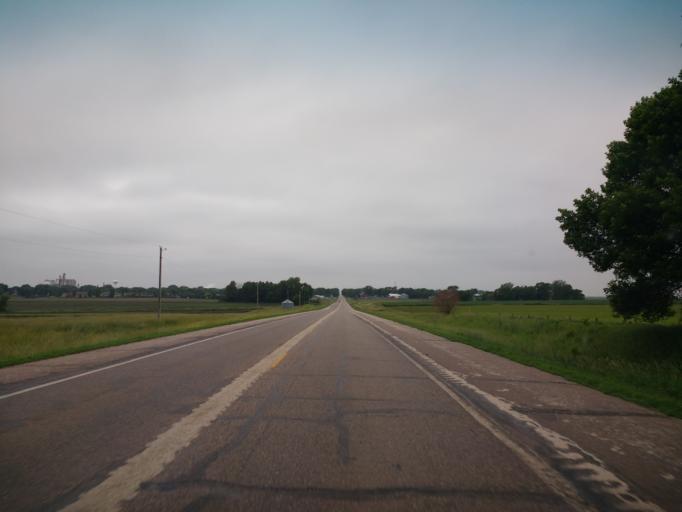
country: US
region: Iowa
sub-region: O'Brien County
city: Hartley
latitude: 43.1848
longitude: -95.4540
